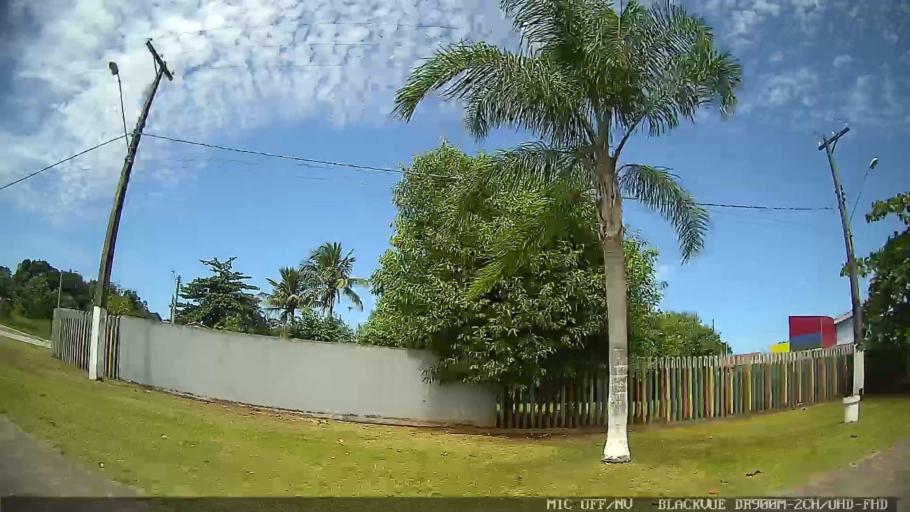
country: BR
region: Sao Paulo
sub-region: Iguape
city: Iguape
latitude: -24.7347
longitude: -47.5448
